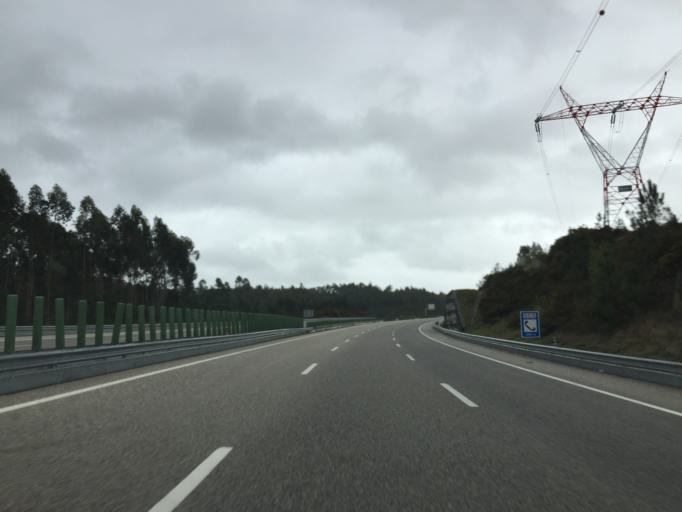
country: PT
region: Leiria
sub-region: Pombal
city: Lourical
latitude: 39.9527
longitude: -8.7721
